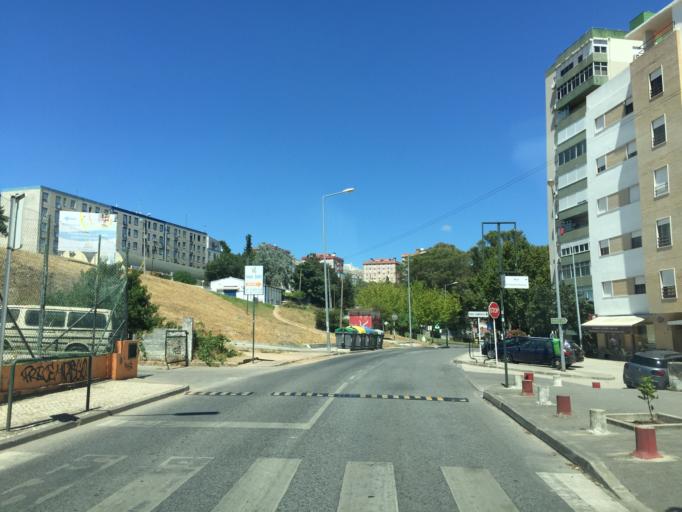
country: PT
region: Lisbon
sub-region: Odivelas
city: Povoa de Santo Adriao
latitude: 38.8108
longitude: -9.1624
